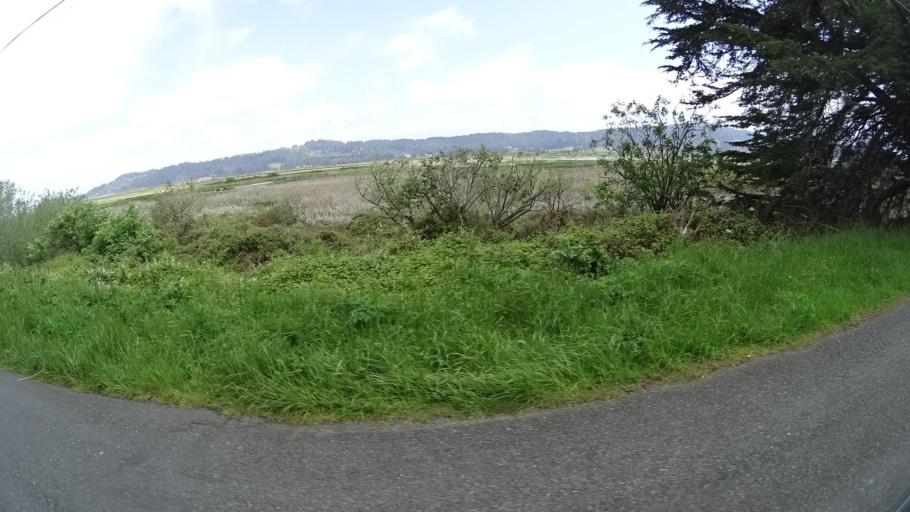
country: US
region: California
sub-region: Humboldt County
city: Humboldt Hill
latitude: 40.6852
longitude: -124.2326
